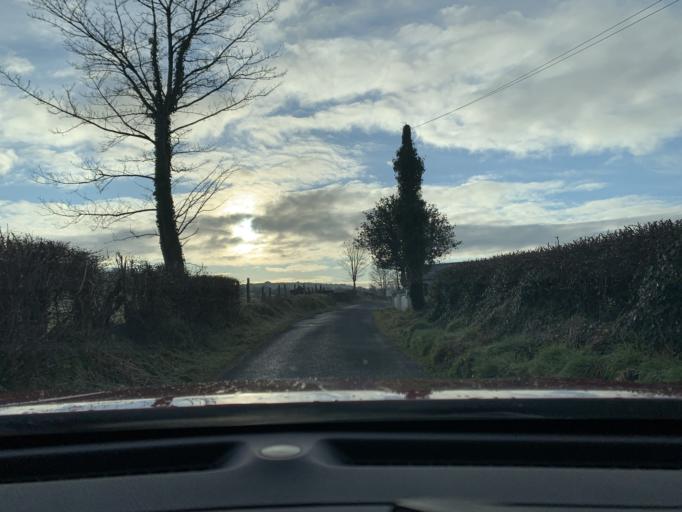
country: IE
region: Connaught
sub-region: Sligo
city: Ballymote
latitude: 54.1179
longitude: -8.5348
